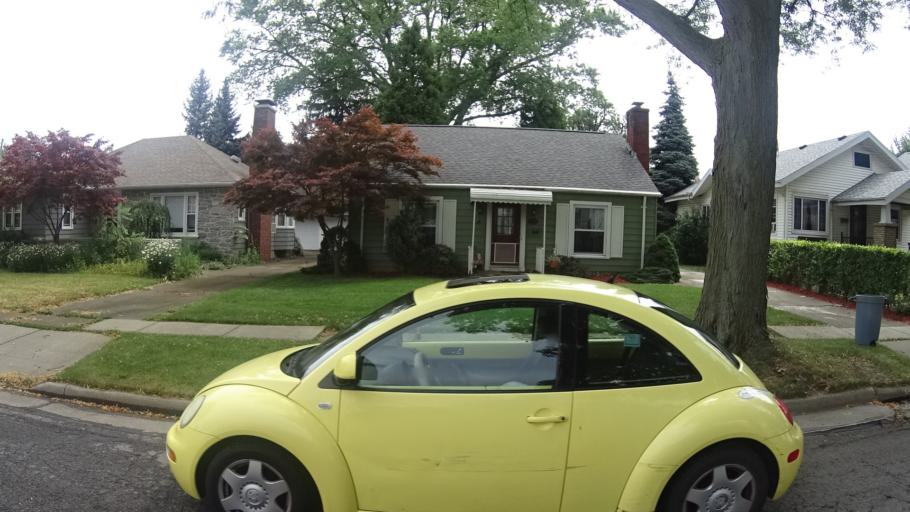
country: US
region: Ohio
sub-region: Erie County
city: Sandusky
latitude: 41.4461
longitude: -82.6942
